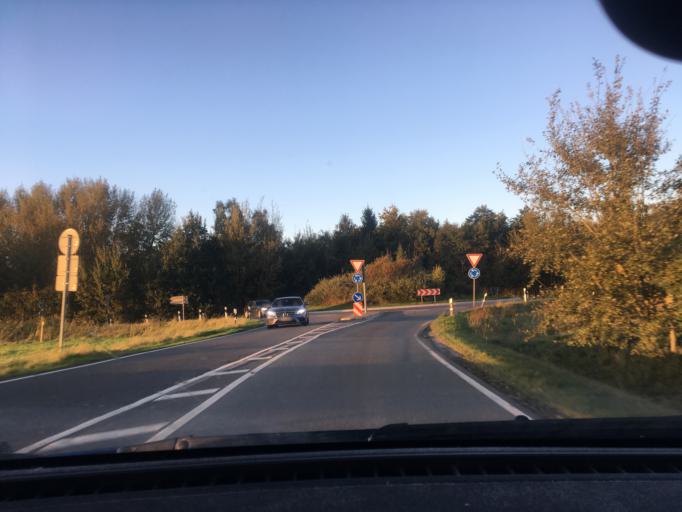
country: DE
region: Lower Saxony
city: Barendorf
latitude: 53.2296
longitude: 10.5141
